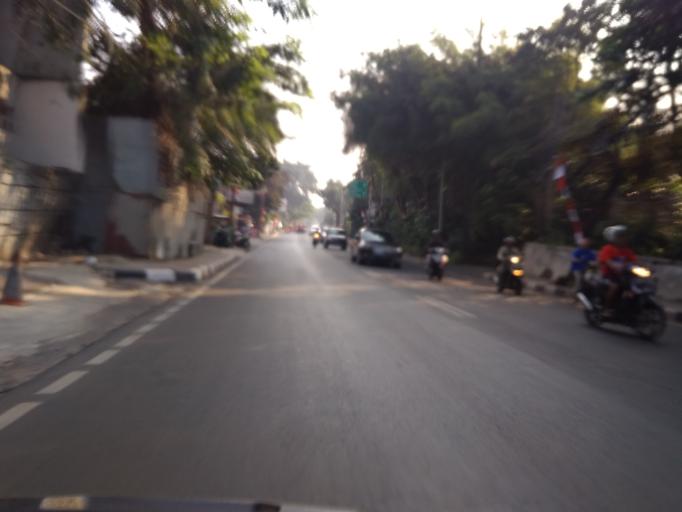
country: ID
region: Jakarta Raya
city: Jakarta
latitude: -6.2769
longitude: 106.8204
